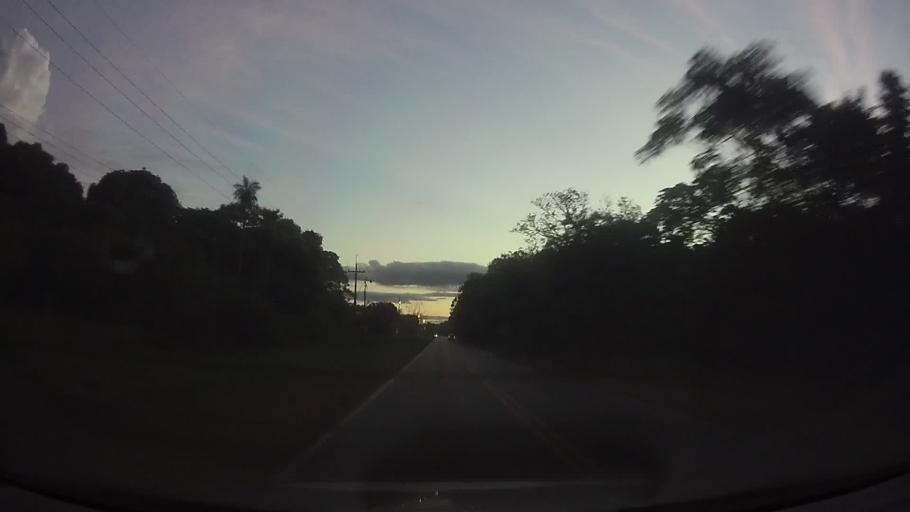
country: PY
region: Central
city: Itaugua
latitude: -25.4111
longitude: -57.3602
